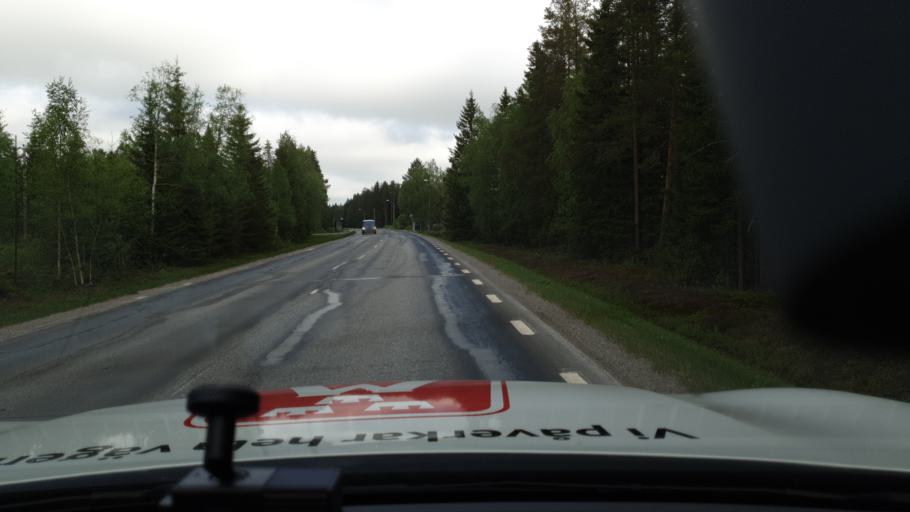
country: SE
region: Vaesterbotten
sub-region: Umea Kommun
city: Roback
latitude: 63.8794
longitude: 20.1991
